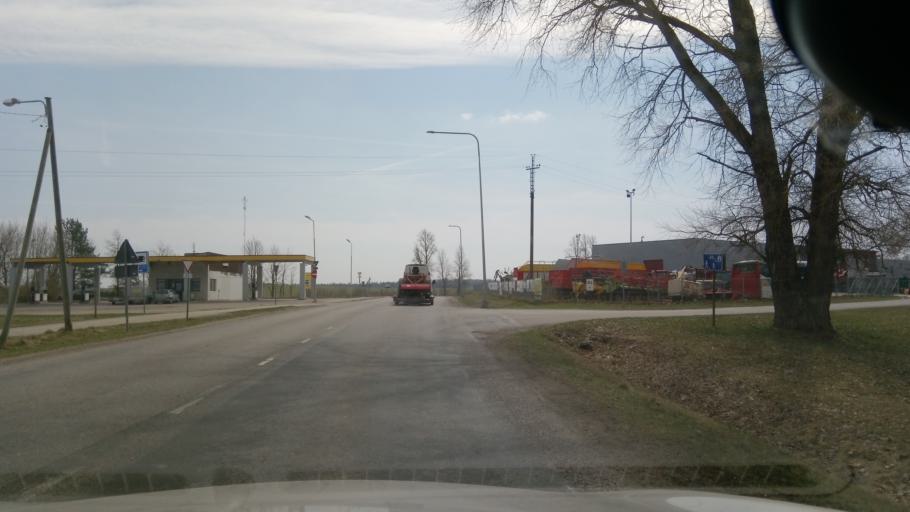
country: EE
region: Jaervamaa
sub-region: Tueri vald
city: Sarevere
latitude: 58.7828
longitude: 25.4348
